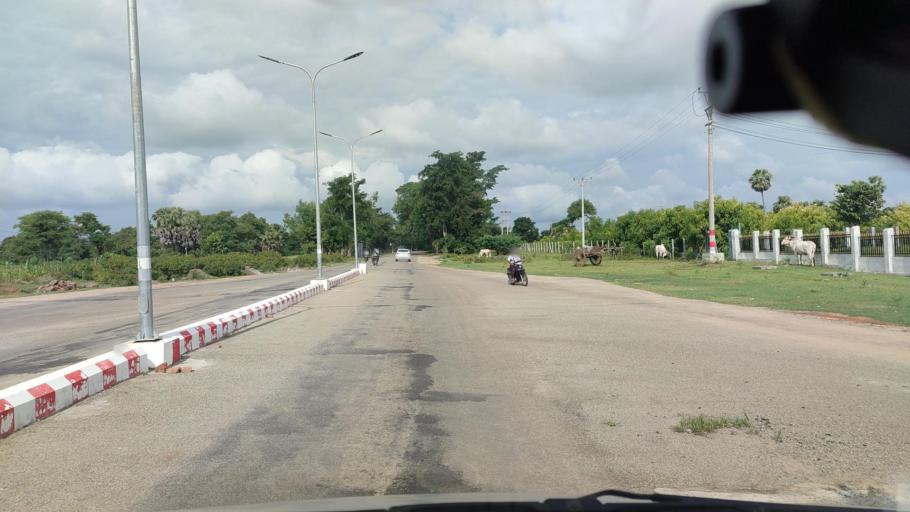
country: MM
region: Mandalay
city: Meiktila
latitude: 21.1537
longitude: 95.6094
